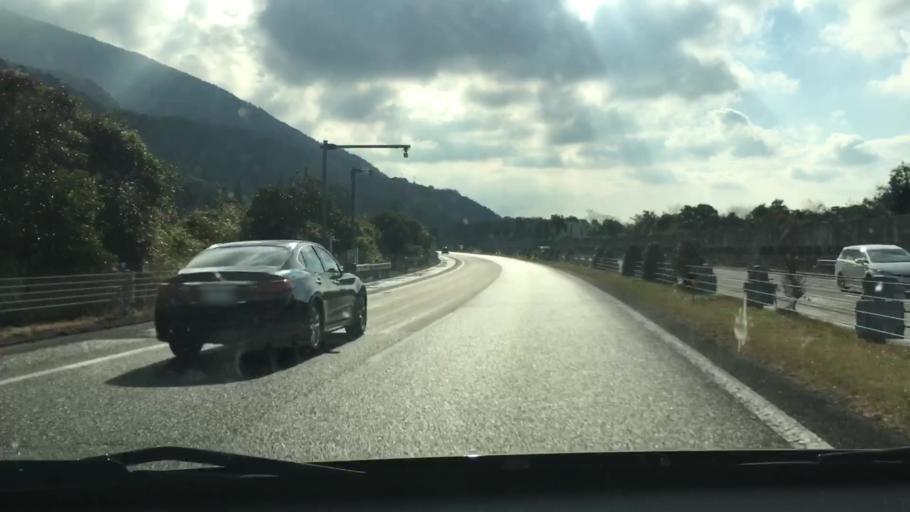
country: JP
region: Kumamoto
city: Yatsushiro
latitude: 32.5376
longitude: 130.6736
